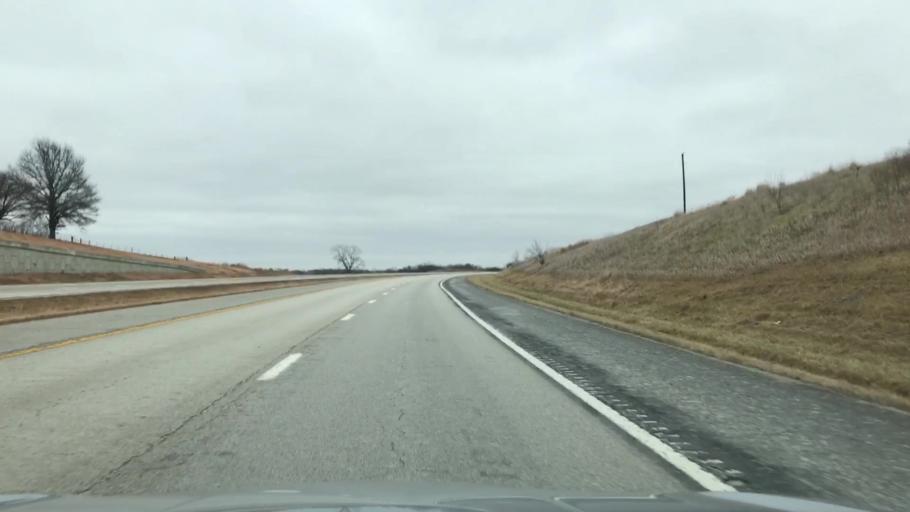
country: US
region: Missouri
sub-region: Caldwell County
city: Hamilton
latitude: 39.7486
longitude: -94.0545
